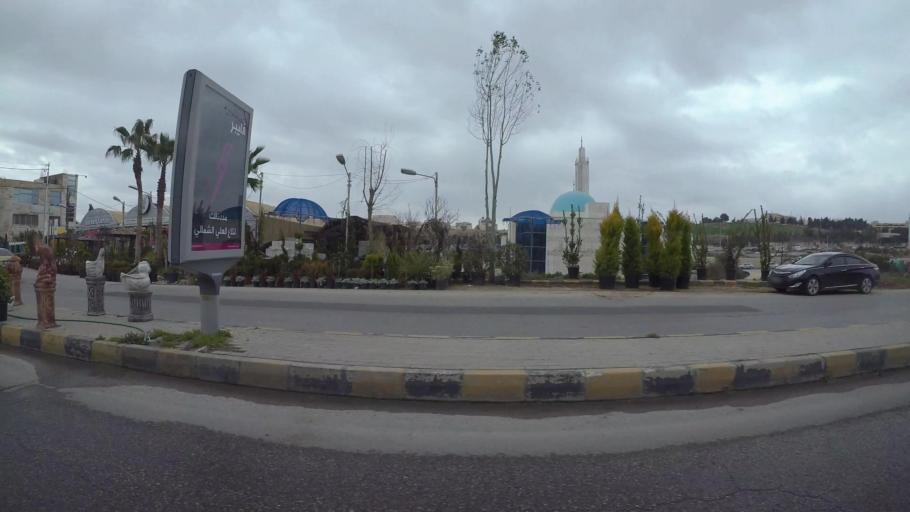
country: JO
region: Amman
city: Wadi as Sir
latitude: 31.9753
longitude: 35.8407
